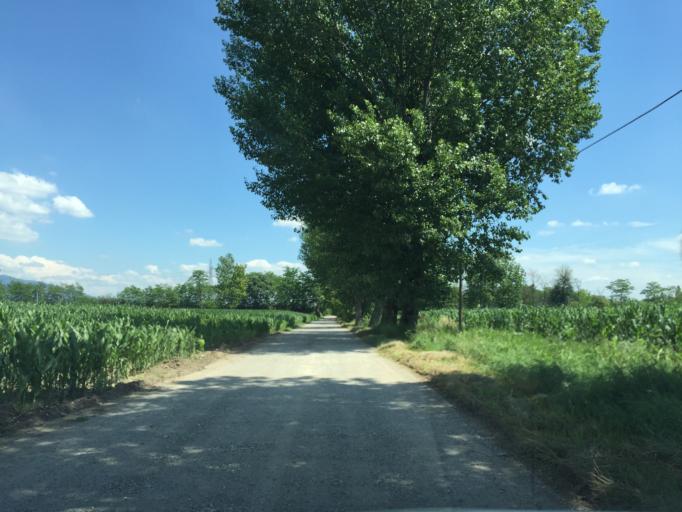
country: IT
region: Lombardy
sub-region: Provincia di Brescia
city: Torbole Casaglia
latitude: 45.5224
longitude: 10.1220
